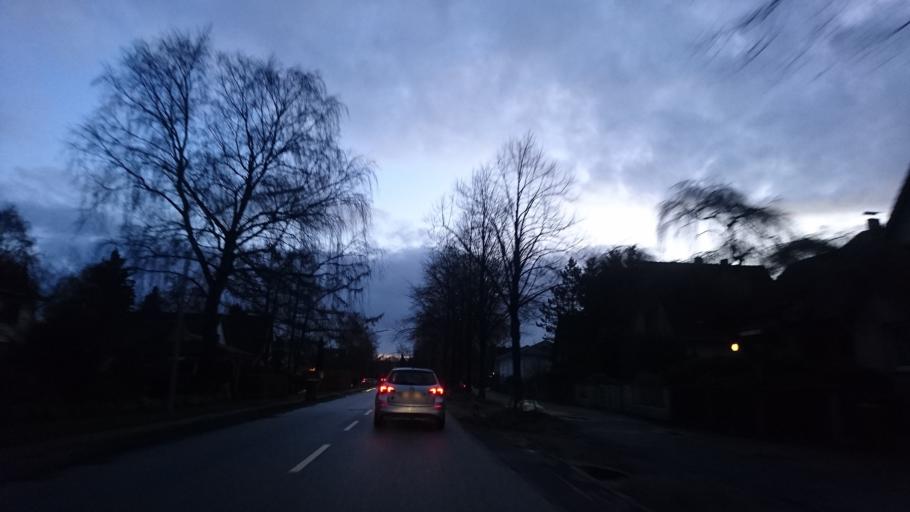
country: DE
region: Hamburg
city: Eidelstedt
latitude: 53.6251
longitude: 9.8964
